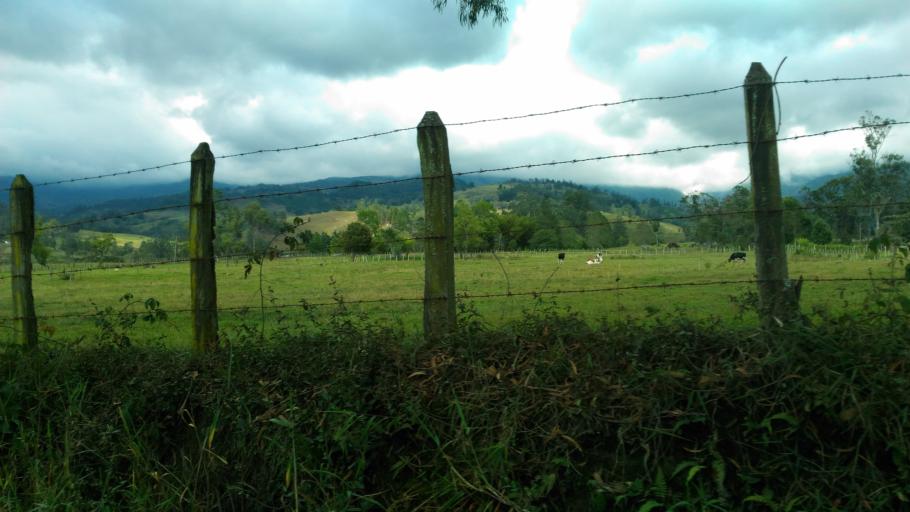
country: CO
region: Cundinamarca
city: Pacho
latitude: 5.1693
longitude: -74.1243
